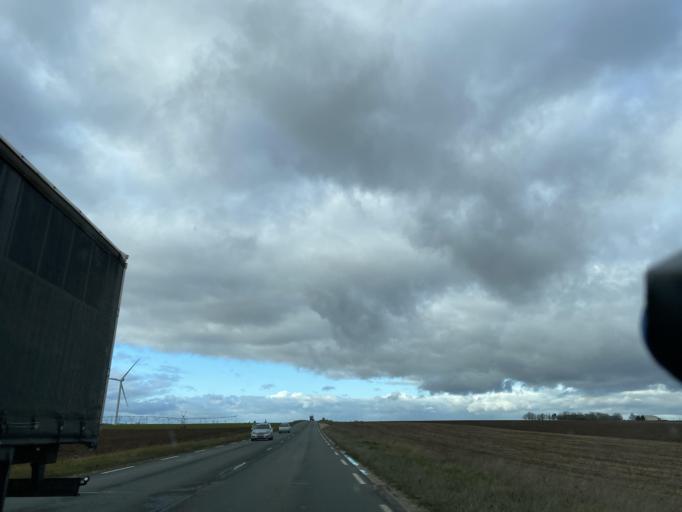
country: FR
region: Centre
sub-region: Departement d'Eure-et-Loir
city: Janville
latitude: 48.2393
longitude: 1.7818
